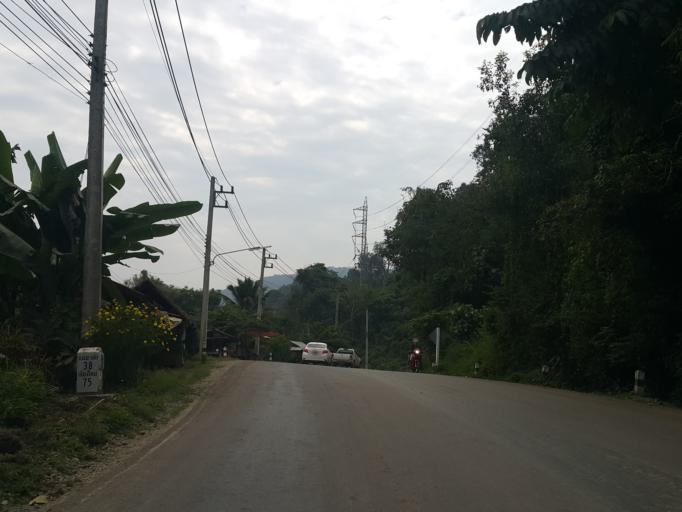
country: TH
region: Chiang Mai
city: Mae Taeng
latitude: 19.1729
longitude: 98.6919
